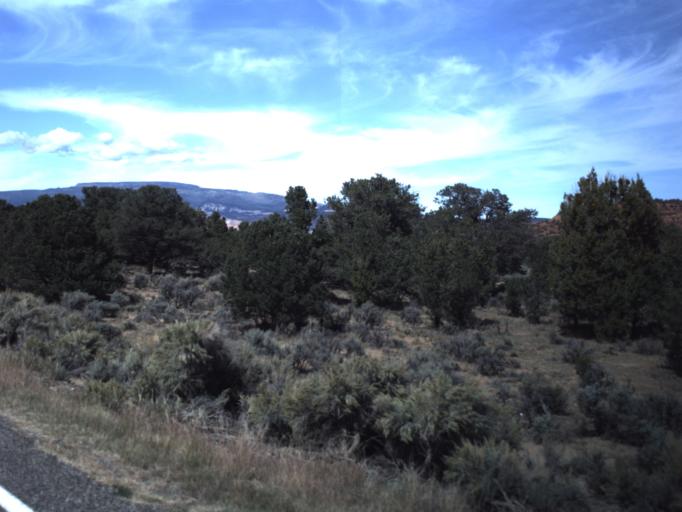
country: US
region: Utah
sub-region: Wayne County
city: Loa
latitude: 38.2382
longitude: -111.3738
